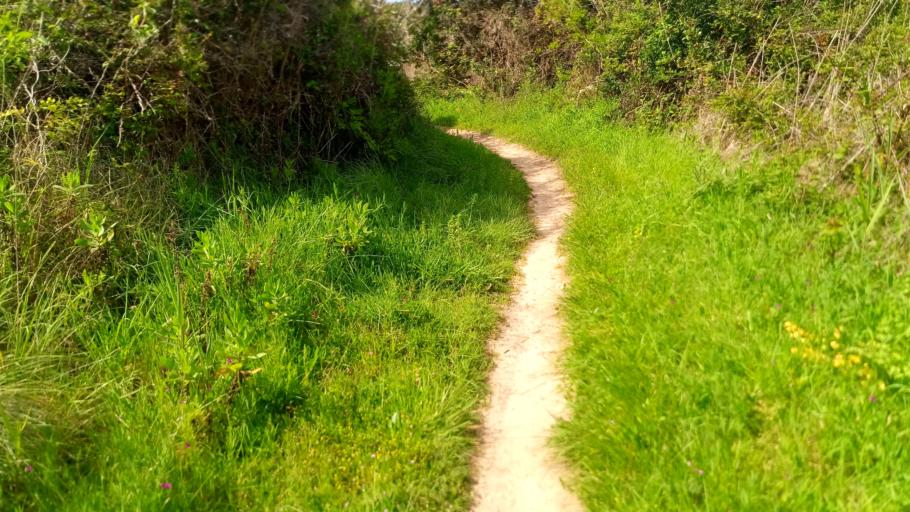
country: PT
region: Leiria
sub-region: Caldas da Rainha
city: Caldas da Rainha
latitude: 39.4004
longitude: -9.1887
